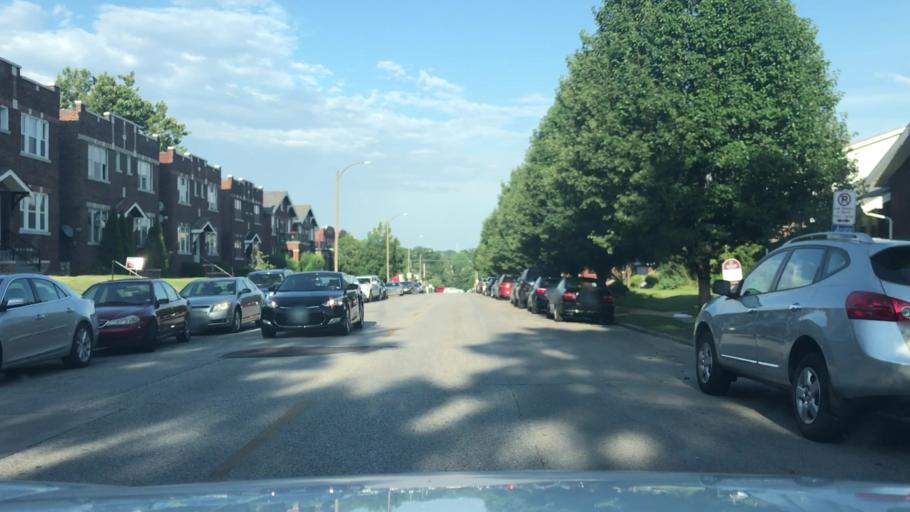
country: US
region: Missouri
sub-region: Saint Louis County
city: Lemay
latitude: 38.5812
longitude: -90.2813
